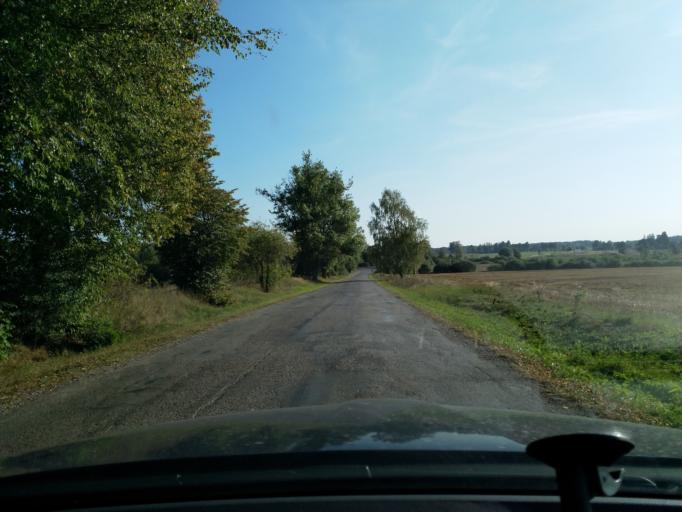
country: LV
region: Aizpute
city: Aizpute
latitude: 56.7981
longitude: 21.6656
